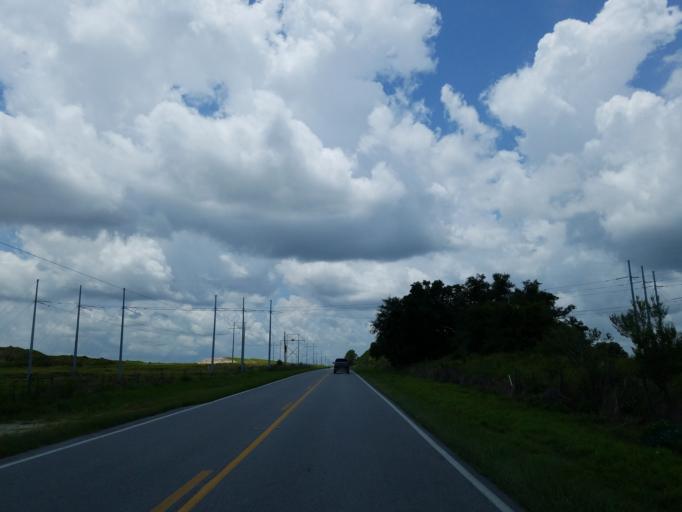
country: US
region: Florida
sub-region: Polk County
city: Mulberry
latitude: 27.8509
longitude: -82.0037
